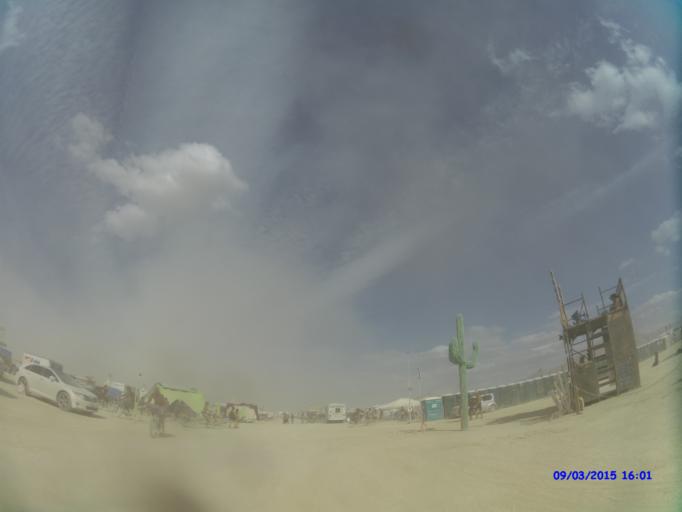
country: US
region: Nevada
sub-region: Pershing County
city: Lovelock
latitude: 40.7773
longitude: -119.2036
